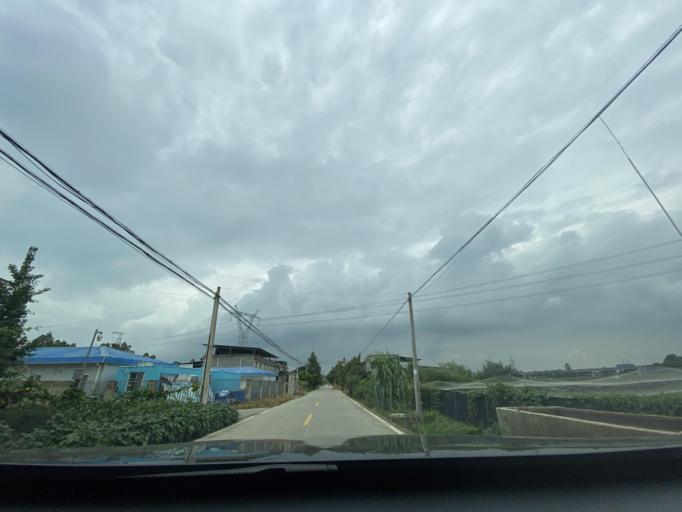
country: CN
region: Sichuan
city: Wujin
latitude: 30.3805
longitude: 103.9679
